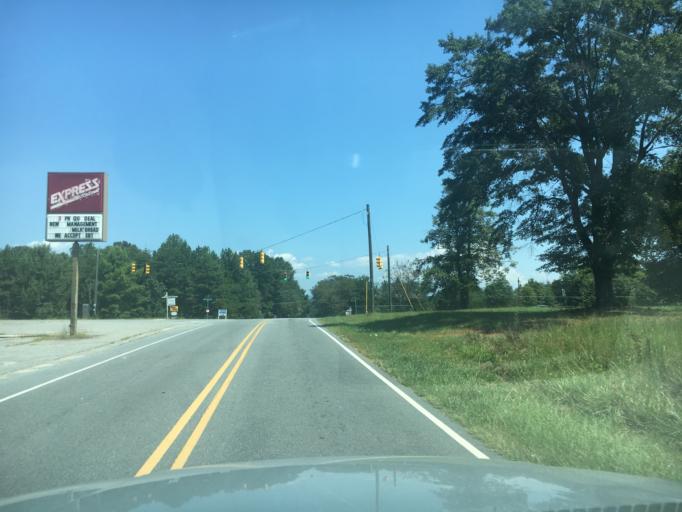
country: US
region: North Carolina
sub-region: Rutherford County
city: Forest City
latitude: 35.3140
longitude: -81.8847
